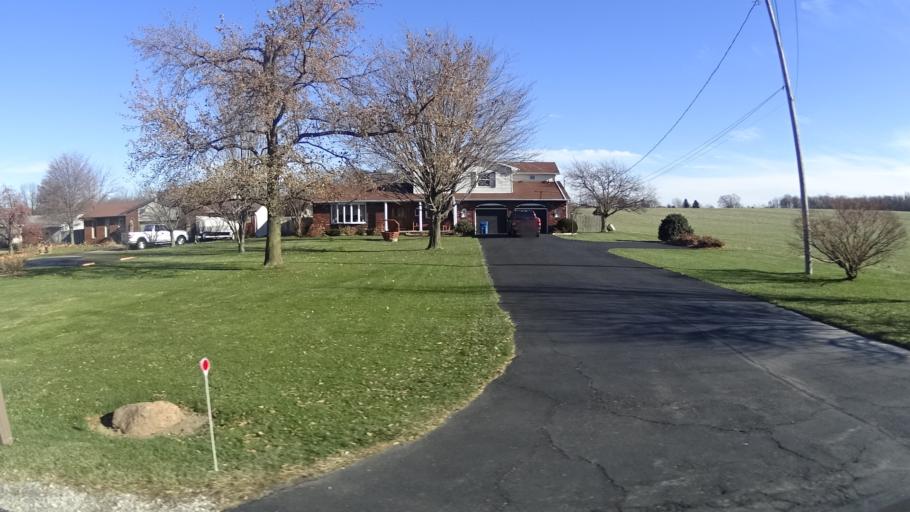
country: US
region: Ohio
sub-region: Lorain County
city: South Amherst
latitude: 41.3785
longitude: -82.2821
